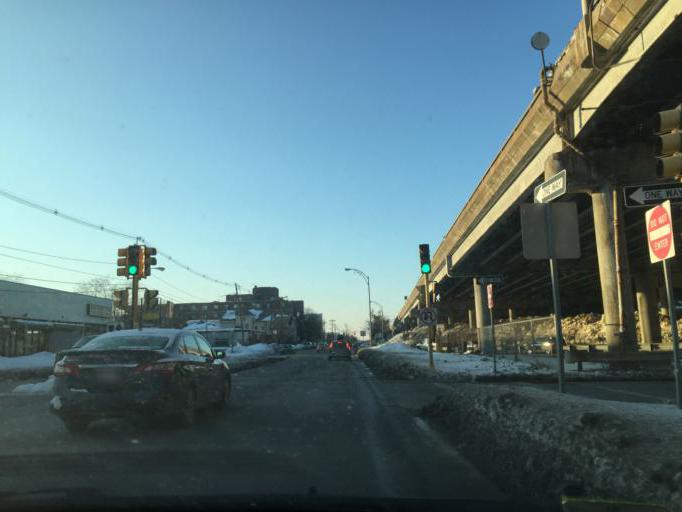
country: US
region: Massachusetts
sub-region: Middlesex County
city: Somerville
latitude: 42.3941
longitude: -71.0868
